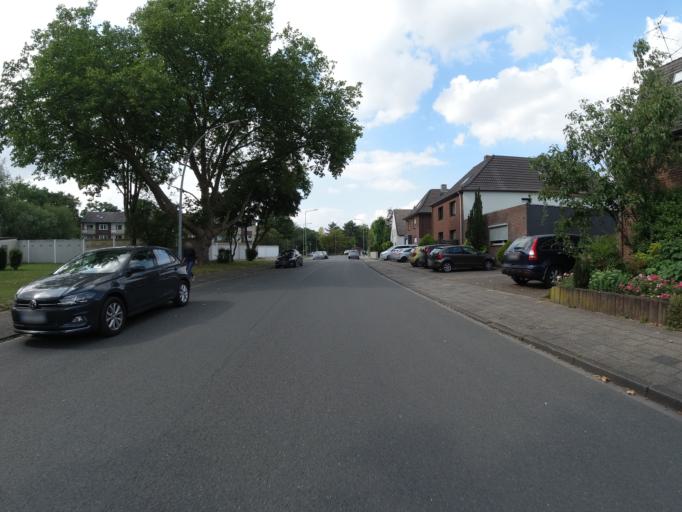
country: DE
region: North Rhine-Westphalia
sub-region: Regierungsbezirk Dusseldorf
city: Moers
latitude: 51.3970
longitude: 6.6750
